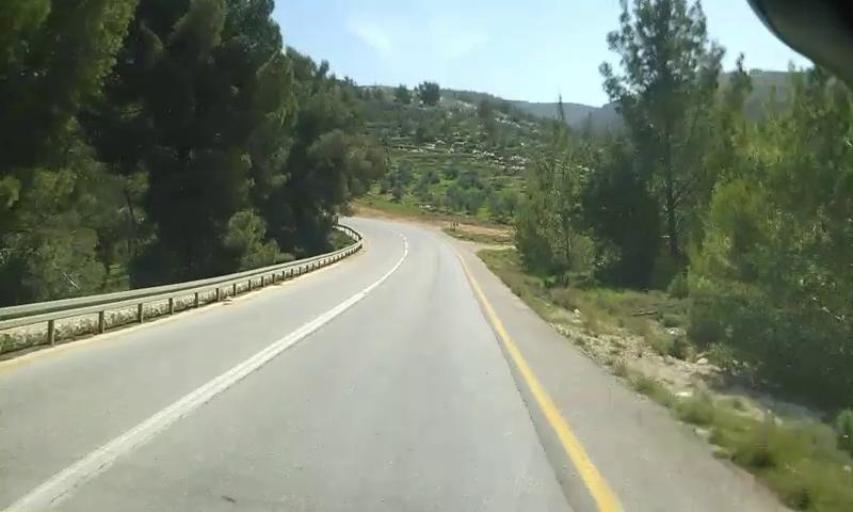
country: PS
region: West Bank
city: Nahhalin
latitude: 31.6741
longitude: 35.1005
